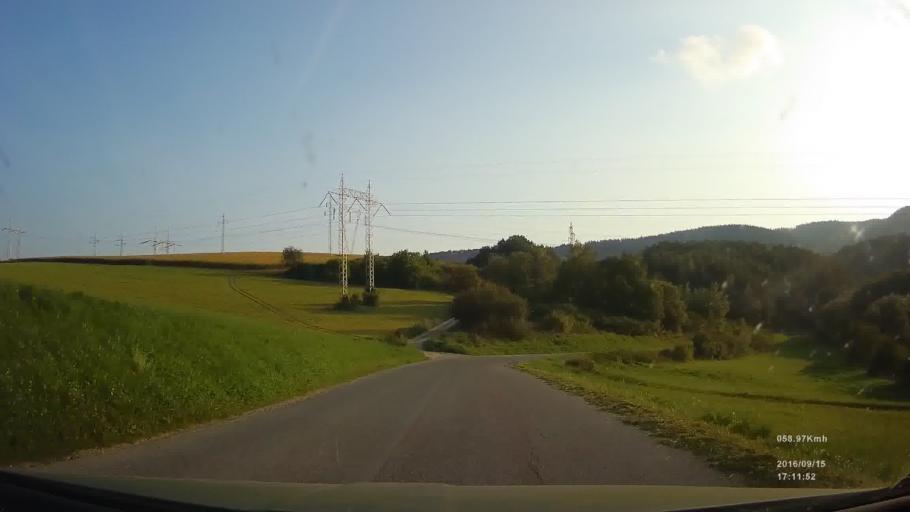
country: SK
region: Presovsky
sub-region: Okres Presov
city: Presov
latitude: 48.9156
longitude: 21.1009
